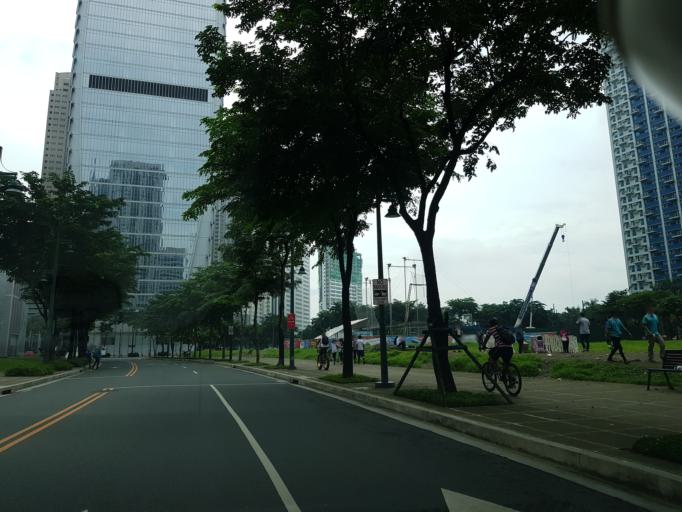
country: PH
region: Metro Manila
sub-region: Makati City
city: Makati City
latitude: 14.5476
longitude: 121.0490
